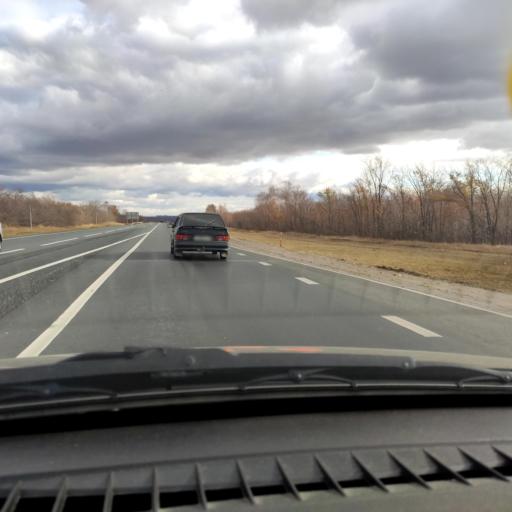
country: RU
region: Samara
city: Syzran'
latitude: 53.2132
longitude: 48.5596
